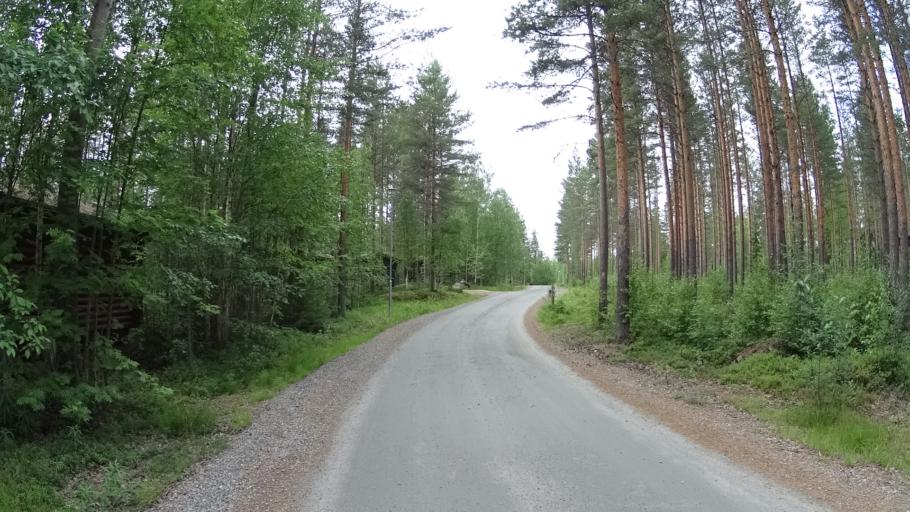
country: FI
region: Southern Ostrobothnia
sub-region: Kuusiokunnat
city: AEhtaeri
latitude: 62.5296
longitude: 24.1915
